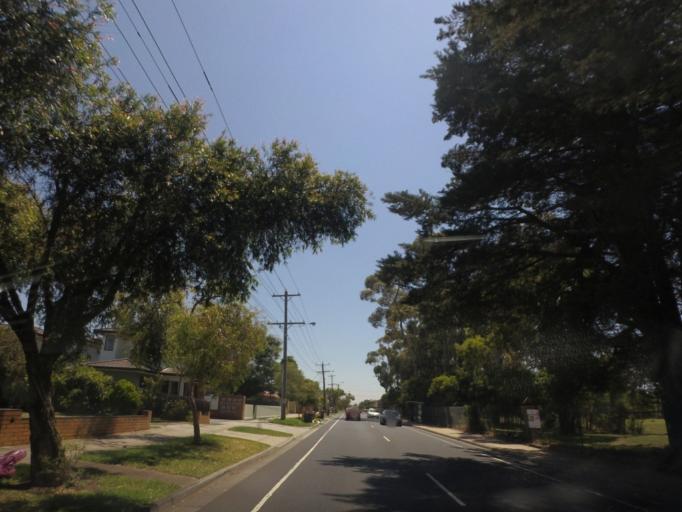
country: AU
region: Victoria
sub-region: Moreland
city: Oak Park
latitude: -37.7156
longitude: 144.9286
